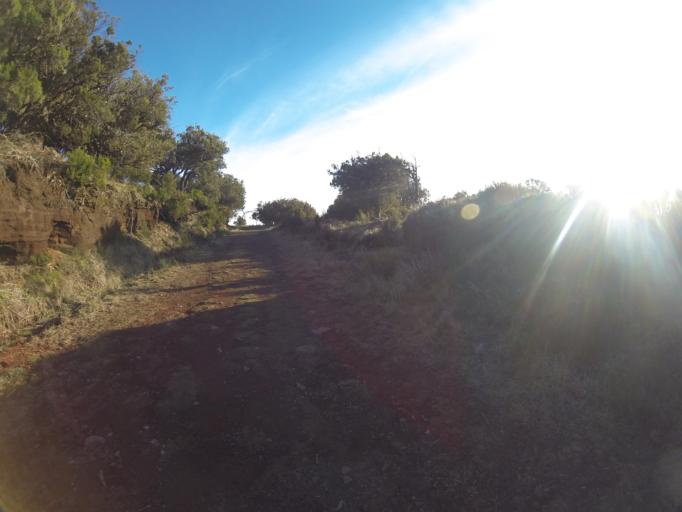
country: PT
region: Madeira
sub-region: Sao Vicente
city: Sao Vicente
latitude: 32.7562
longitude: -17.0571
